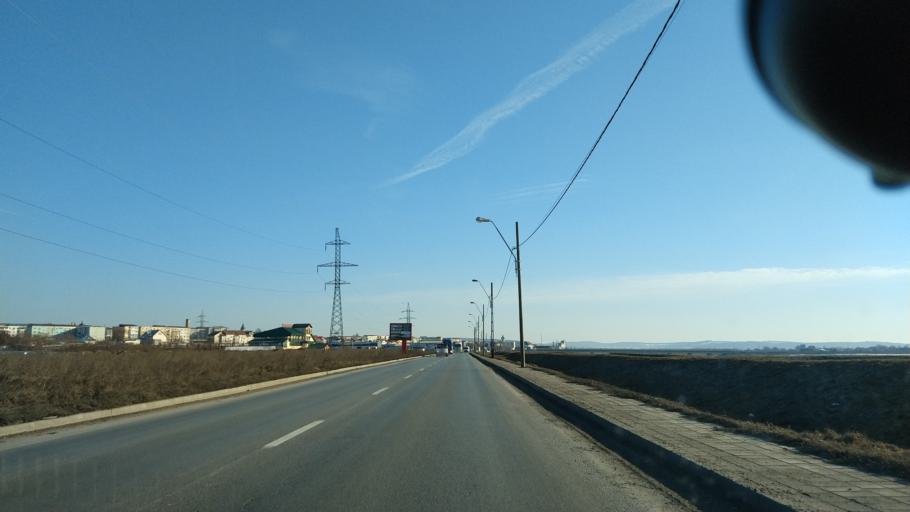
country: RO
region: Neamt
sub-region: Municipiul Roman
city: Roman
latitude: 46.9219
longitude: 26.9133
